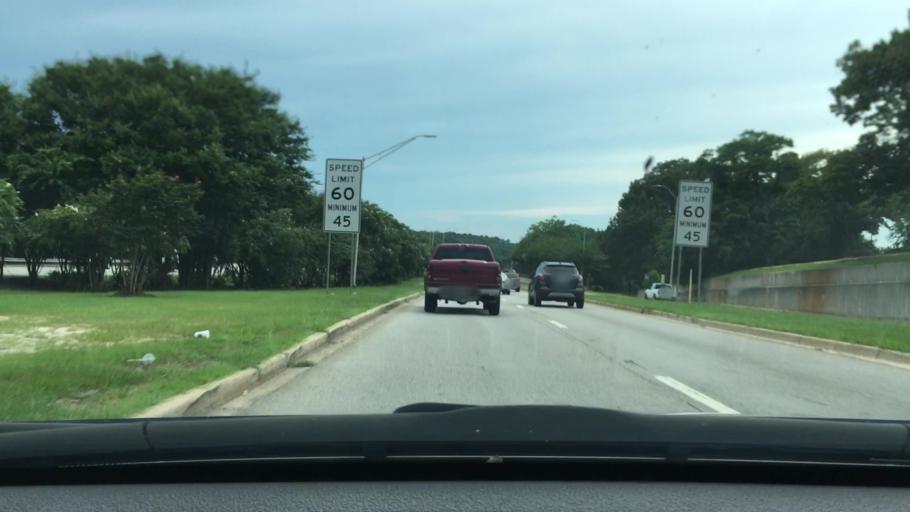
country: US
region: South Carolina
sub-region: Richland County
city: Columbia
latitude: 34.0094
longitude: -81.0516
